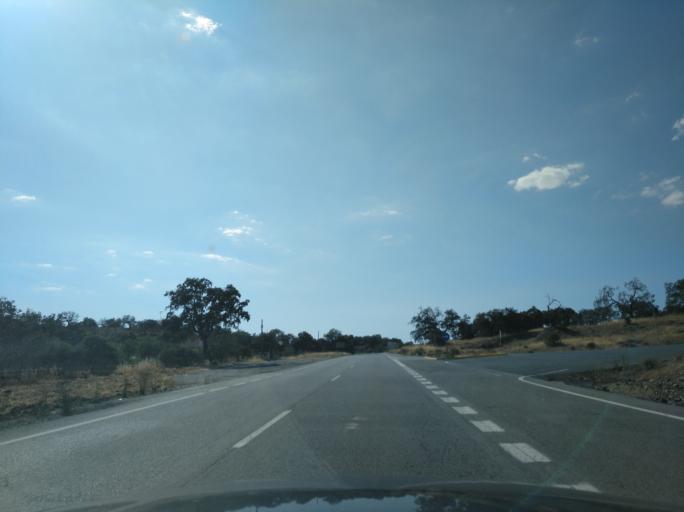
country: ES
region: Andalusia
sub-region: Provincia de Huelva
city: Santa Barbara de Casa
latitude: 37.7911
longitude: -7.1807
